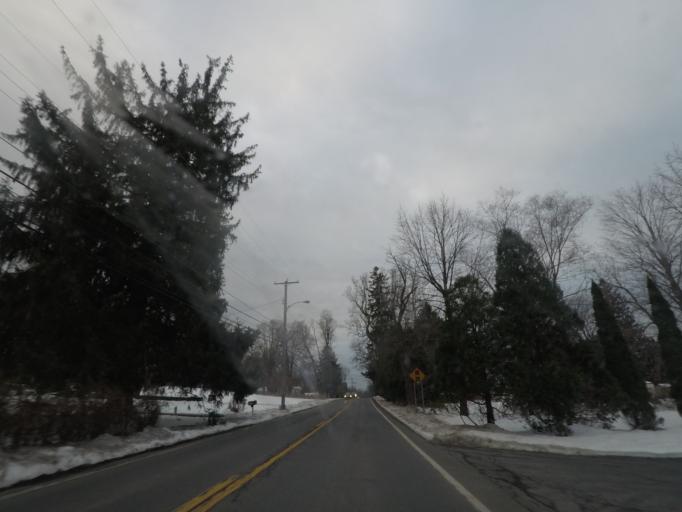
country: US
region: New York
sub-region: Ulster County
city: Clintondale
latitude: 41.6702
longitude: -74.1051
